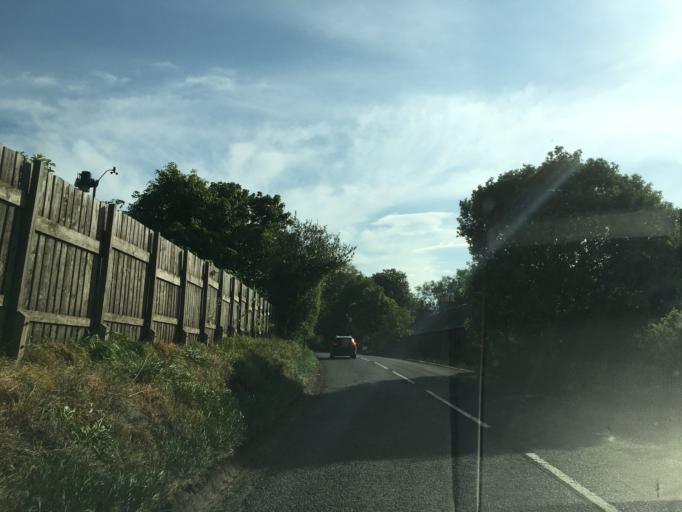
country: GB
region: Scotland
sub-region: The Scottish Borders
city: West Linton
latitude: 55.7252
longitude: -3.3267
